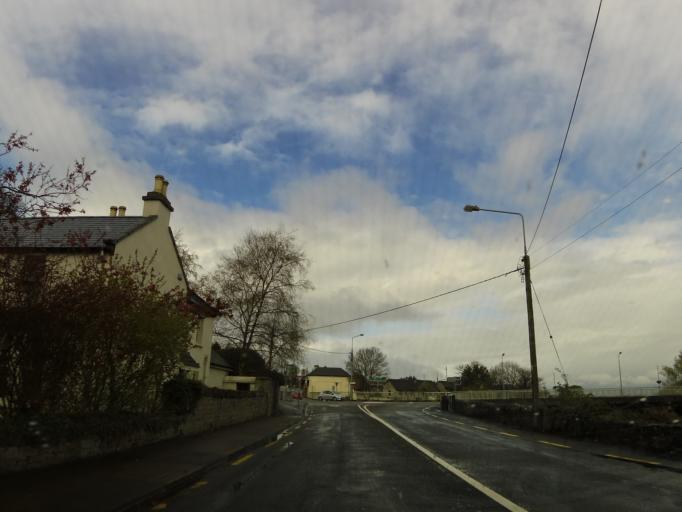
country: IE
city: Ballisodare
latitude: 54.2088
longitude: -8.5091
